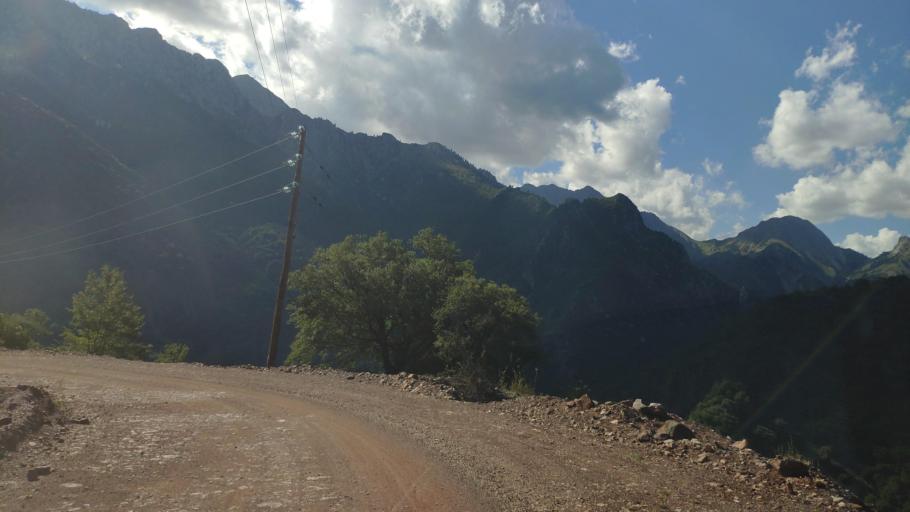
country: GR
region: Central Greece
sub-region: Nomos Evrytanias
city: Kerasochori
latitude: 39.1083
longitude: 21.6118
